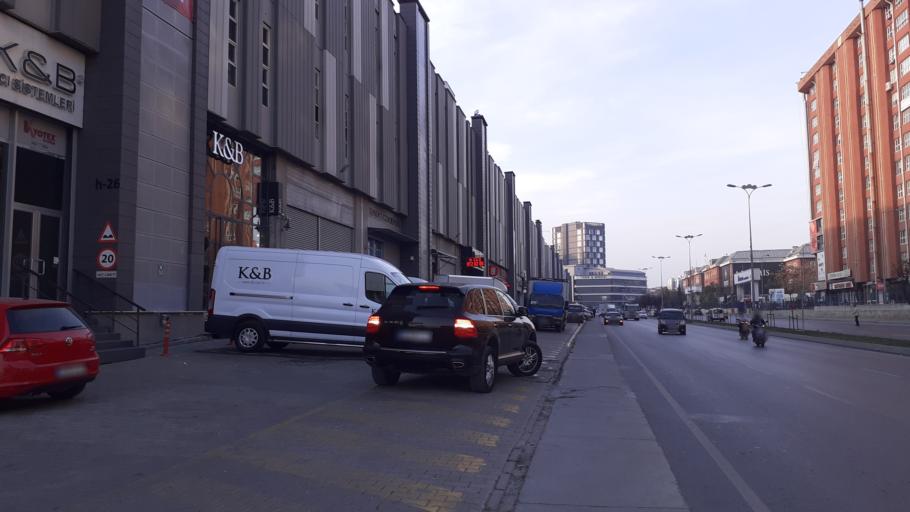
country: TR
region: Istanbul
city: Basaksehir
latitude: 41.0700
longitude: 28.7959
